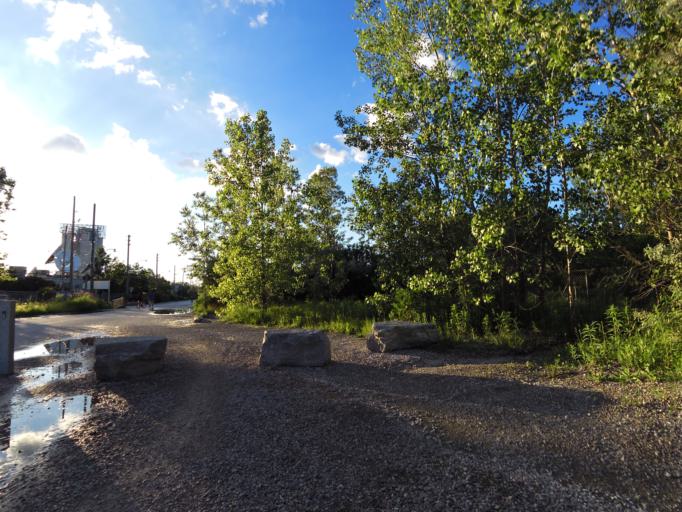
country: CA
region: Ontario
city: Toronto
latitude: 43.6520
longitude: -79.3226
